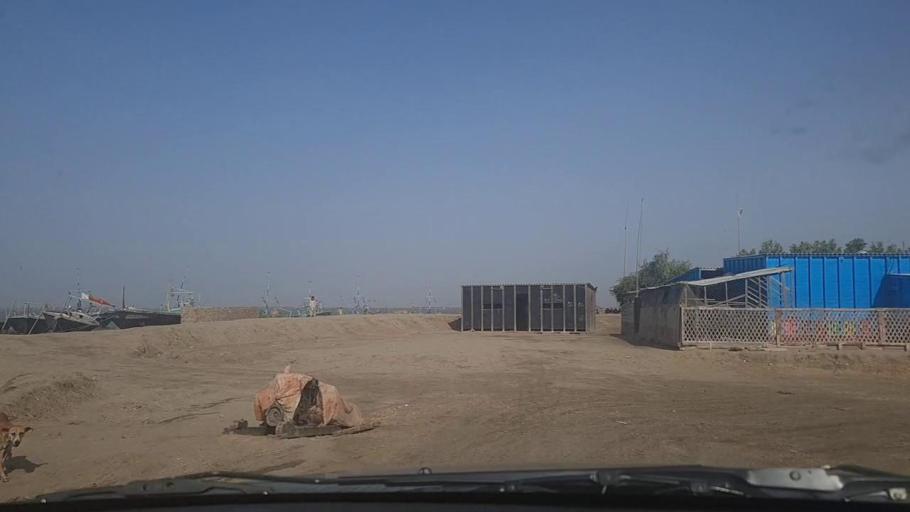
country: PK
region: Sindh
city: Keti Bandar
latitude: 24.1823
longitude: 67.5075
